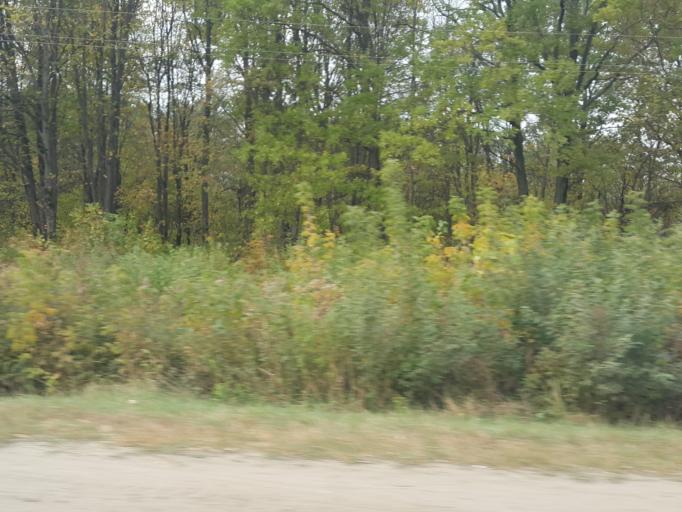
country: RU
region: Tambov
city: Bokino
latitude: 52.6338
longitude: 41.4408
